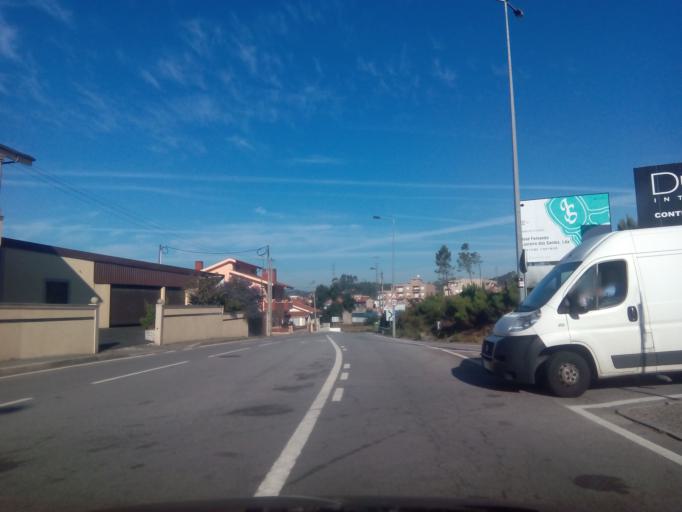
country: PT
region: Porto
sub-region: Paredes
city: Gandra
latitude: 41.2023
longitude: -8.4417
